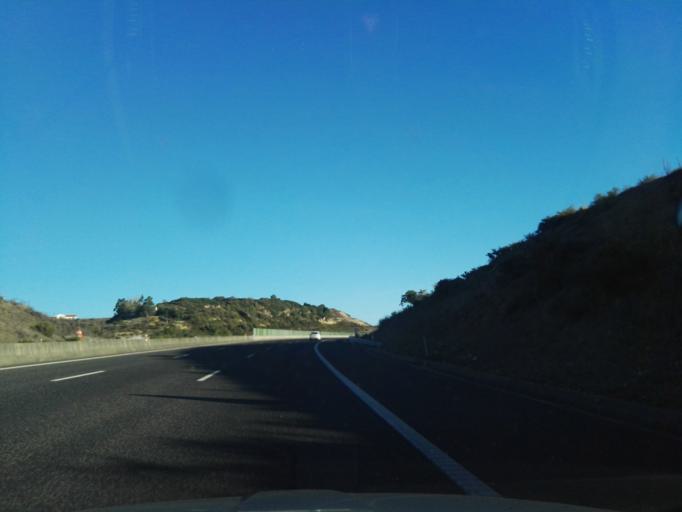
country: PT
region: Lisbon
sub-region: Loures
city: Bucelas
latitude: 38.9230
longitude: -9.0757
